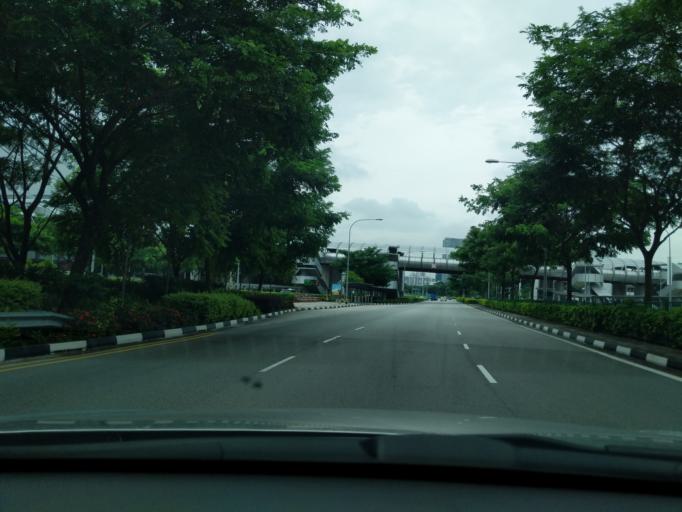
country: SG
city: Singapore
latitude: 1.3068
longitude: 103.8760
